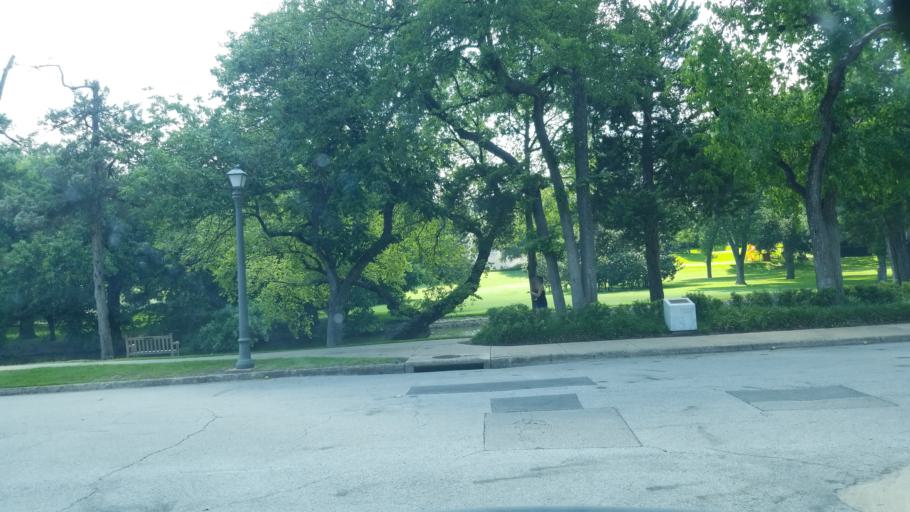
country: US
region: Texas
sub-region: Dallas County
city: Highland Park
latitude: 32.8295
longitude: -96.8019
